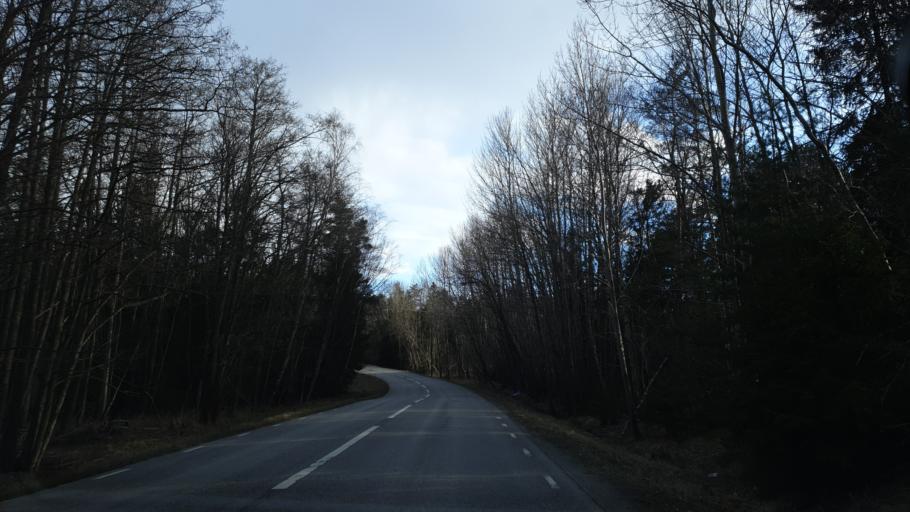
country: SE
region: Stockholm
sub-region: Varmdo Kommun
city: Holo
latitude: 59.3327
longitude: 18.7191
